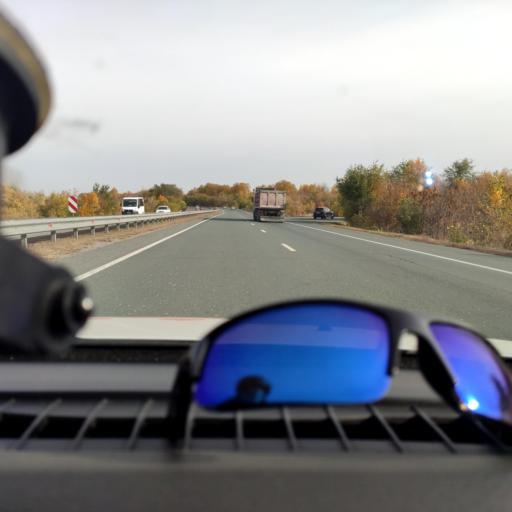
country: RU
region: Samara
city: Novokuybyshevsk
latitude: 53.0263
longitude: 49.9891
